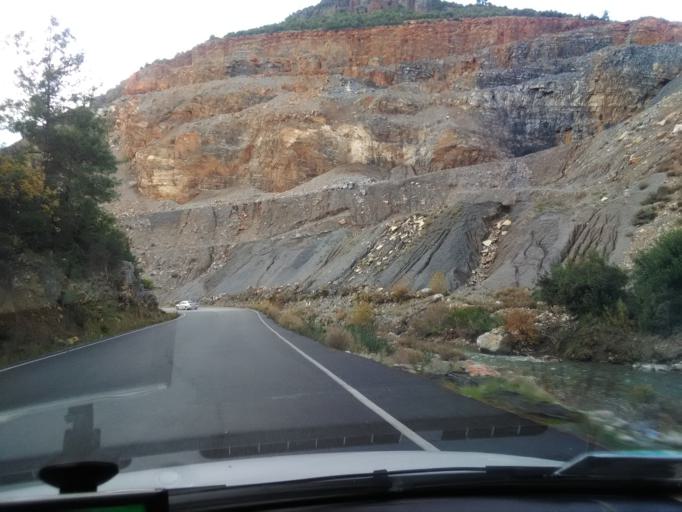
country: TR
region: Antalya
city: Gazipasa
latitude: 36.2824
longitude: 32.3649
